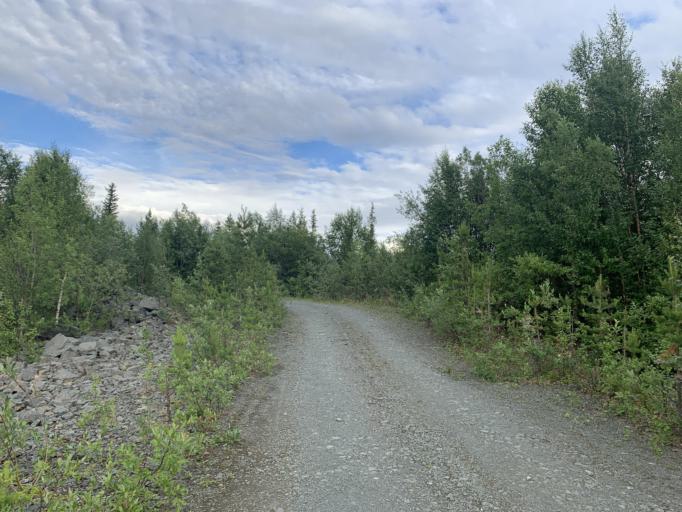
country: RU
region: Murmansk
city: Monchegorsk
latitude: 67.8851
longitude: 33.0420
